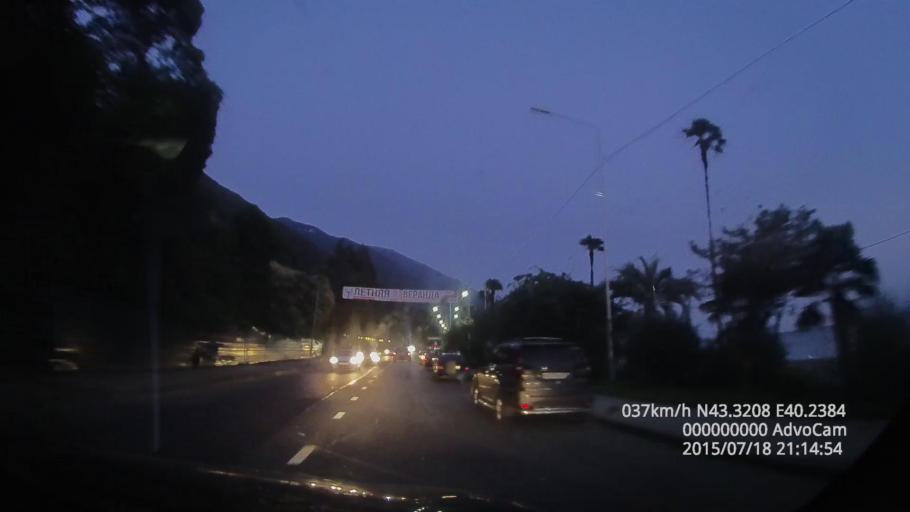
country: GE
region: Abkhazia
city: Gagra
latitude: 43.3207
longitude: 40.2386
